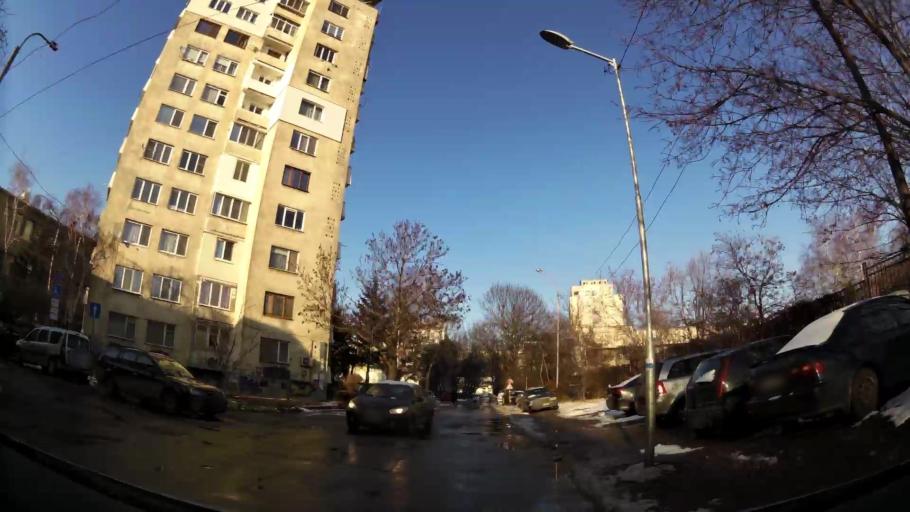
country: BG
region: Sofia-Capital
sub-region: Stolichna Obshtina
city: Sofia
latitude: 42.6765
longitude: 23.3651
